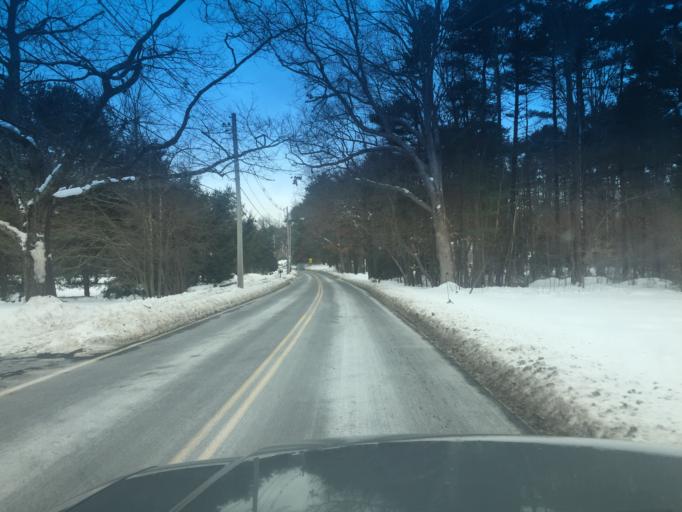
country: US
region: Massachusetts
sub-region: Norfolk County
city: Norfolk
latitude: 42.1096
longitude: -71.2835
